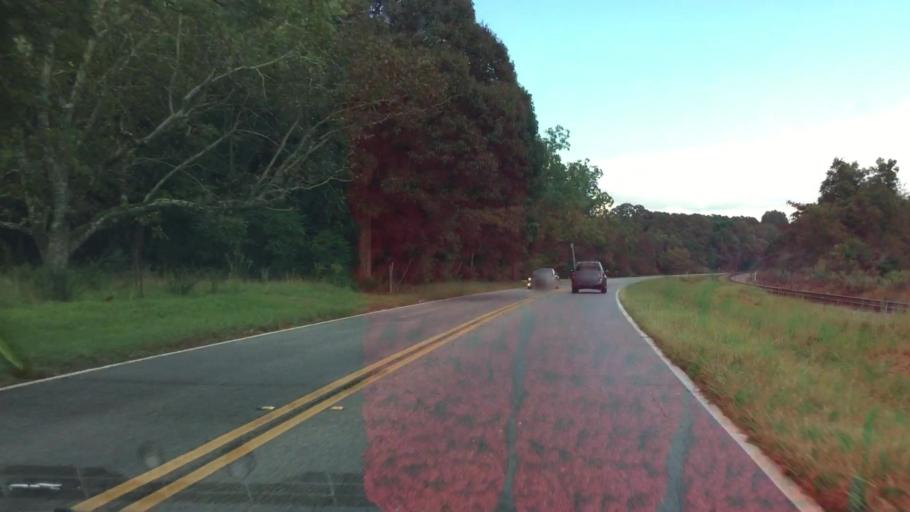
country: US
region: Georgia
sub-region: Clayton County
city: Lovejoy
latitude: 33.4321
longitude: -84.2931
